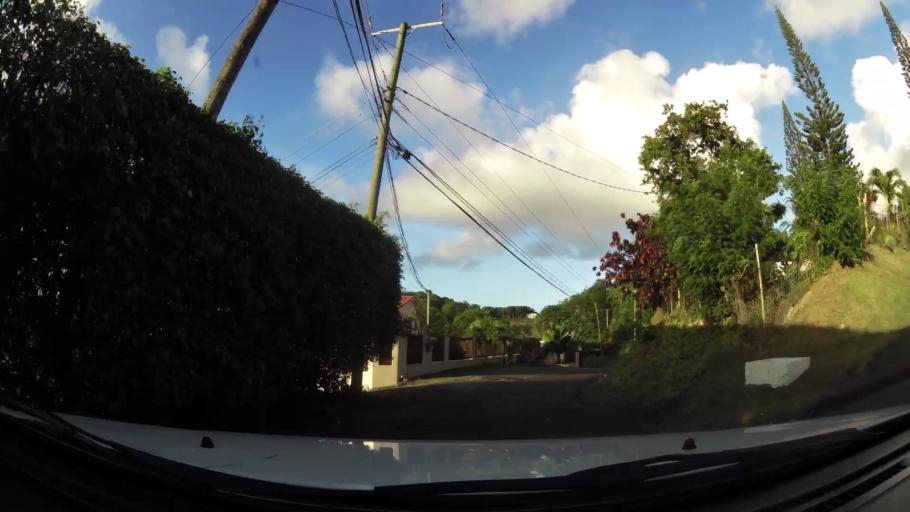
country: LC
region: Gros-Islet
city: Gros Islet
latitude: 14.0651
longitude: -60.9427
